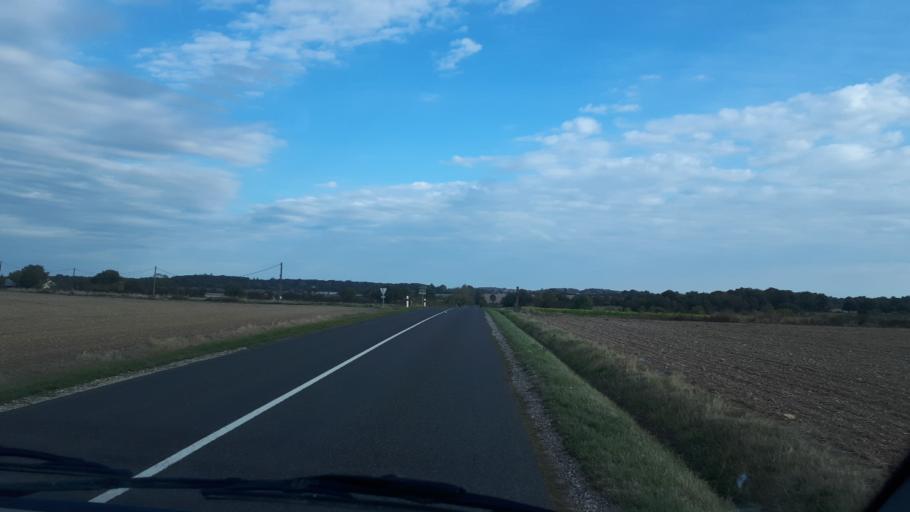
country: FR
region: Centre
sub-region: Departement du Loir-et-Cher
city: Mondoubleau
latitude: 47.9138
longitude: 0.9313
